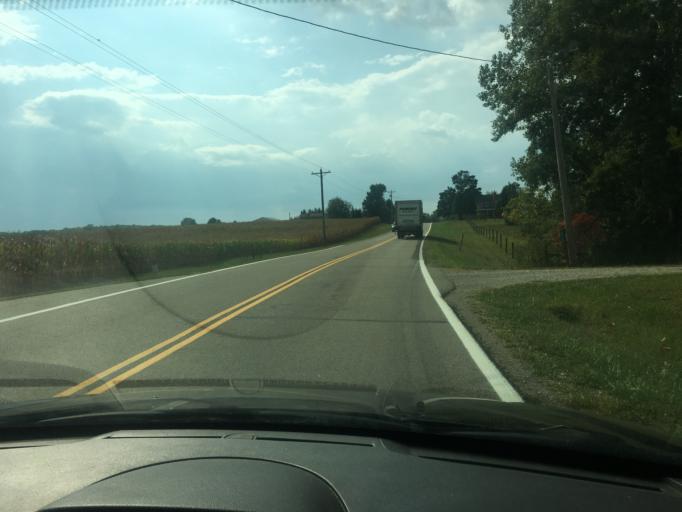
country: US
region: Ohio
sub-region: Champaign County
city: Urbana
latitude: 40.1563
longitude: -83.8279
